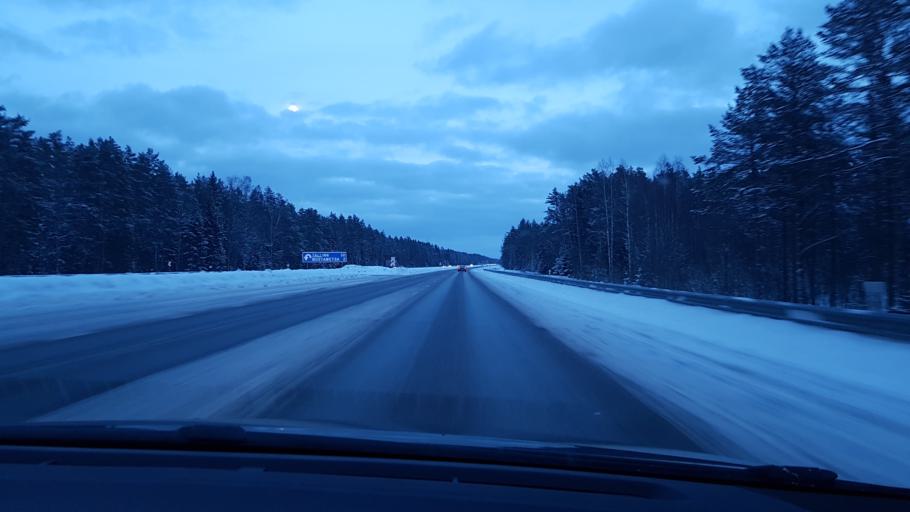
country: EE
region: Harju
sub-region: Kuusalu vald
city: Kuusalu
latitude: 59.4612
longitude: 25.6035
